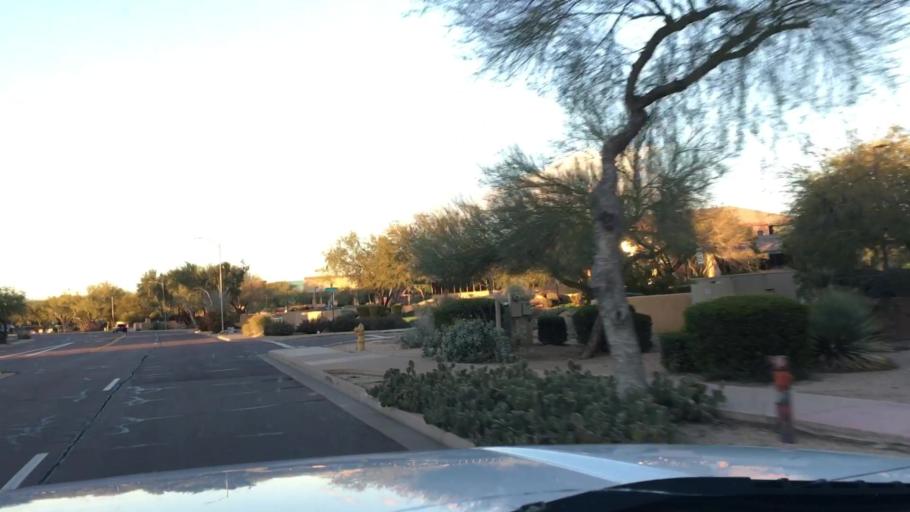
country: US
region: Arizona
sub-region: Maricopa County
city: Paradise Valley
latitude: 33.6413
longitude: -111.8963
